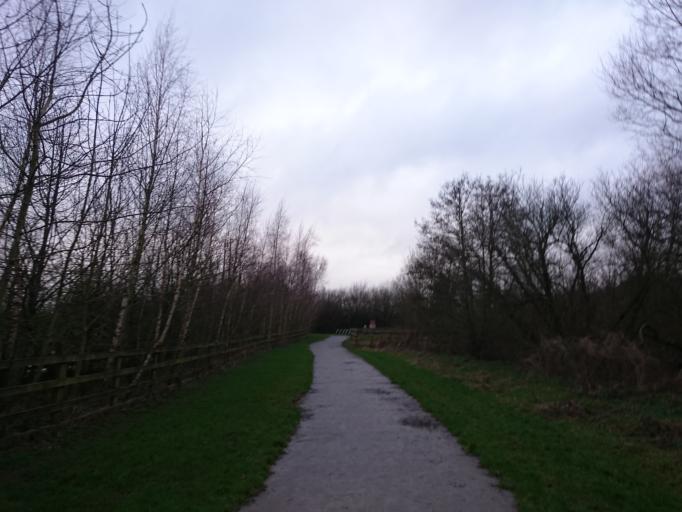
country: IE
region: Leinster
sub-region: Kilkenny
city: Kilkenny
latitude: 52.6743
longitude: -7.2601
